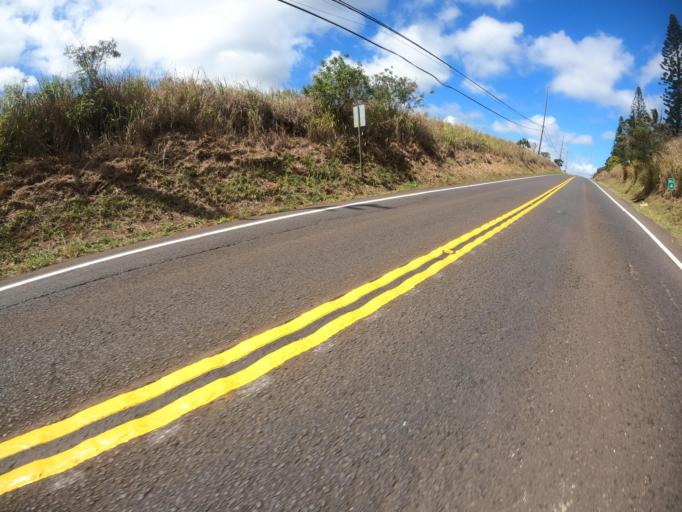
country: US
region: Hawaii
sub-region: Honolulu County
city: Village Park
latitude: 21.4361
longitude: -158.0585
